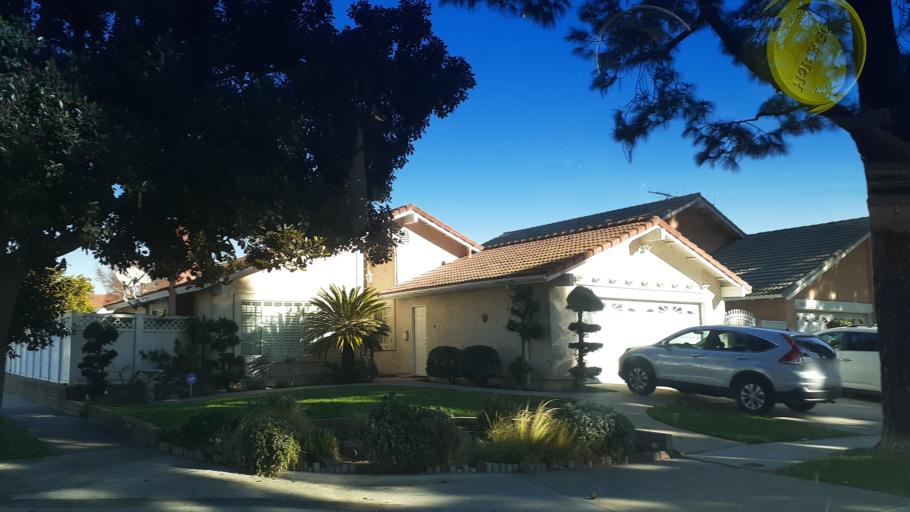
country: US
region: California
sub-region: Los Angeles County
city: Cerritos
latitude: 33.8484
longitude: -118.0652
